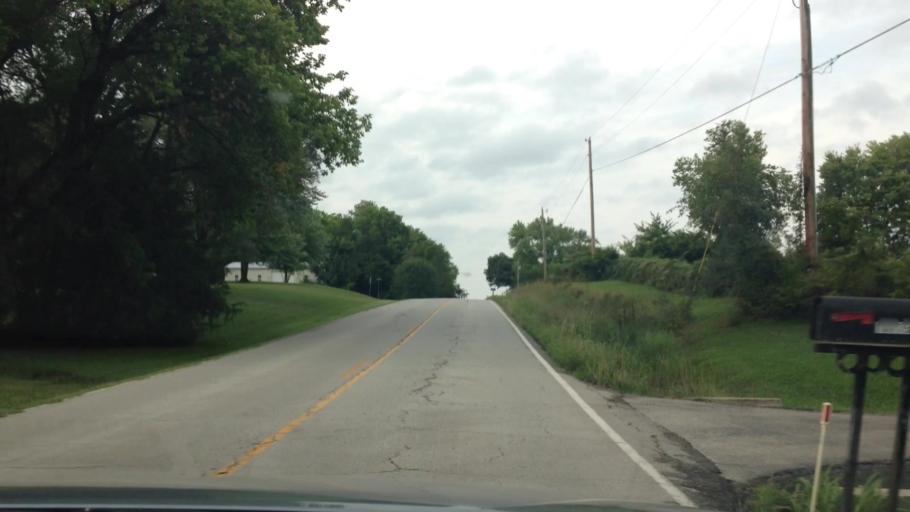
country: US
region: Missouri
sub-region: Clay County
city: Smithville
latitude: 39.3795
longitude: -94.6669
